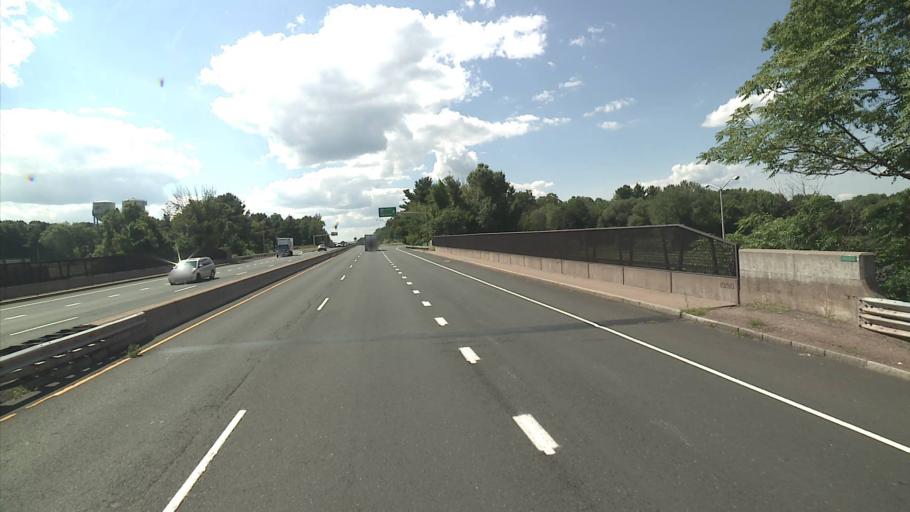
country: US
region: Connecticut
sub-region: Hartford County
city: Thompsonville
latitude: 41.9903
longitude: -72.5873
